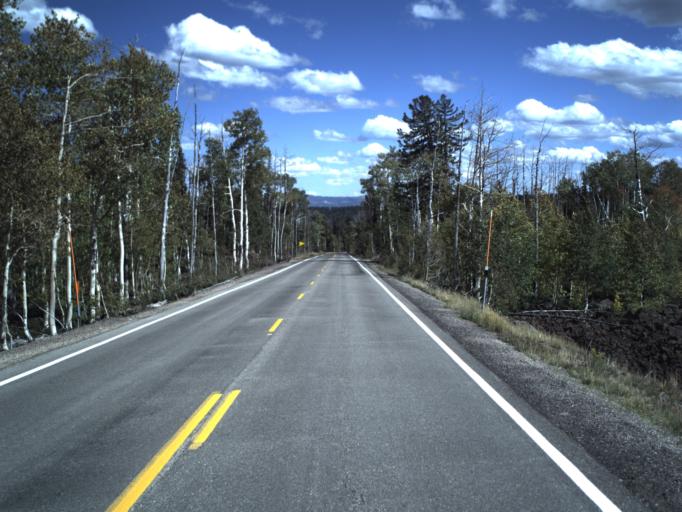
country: US
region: Utah
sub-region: Iron County
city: Parowan
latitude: 37.5179
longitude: -112.7168
